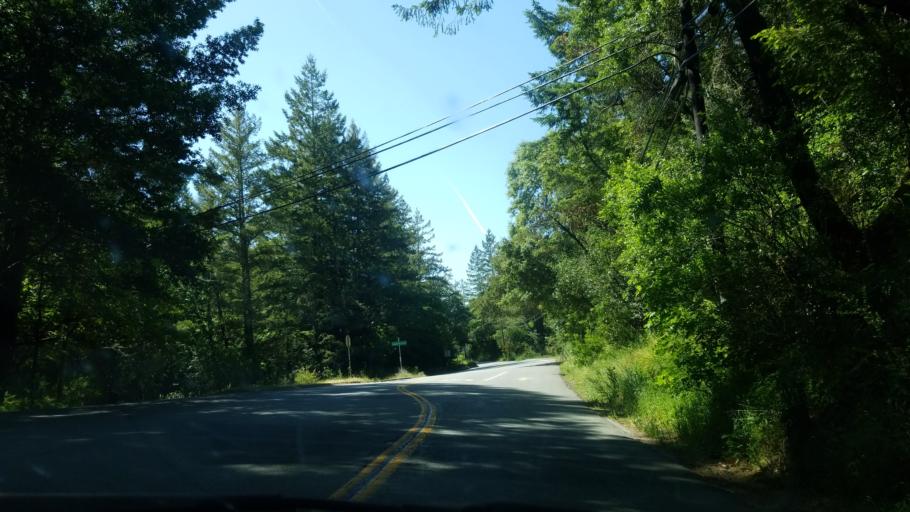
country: US
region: California
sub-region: Santa Clara County
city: Lexington Hills
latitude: 37.1184
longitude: -121.9250
